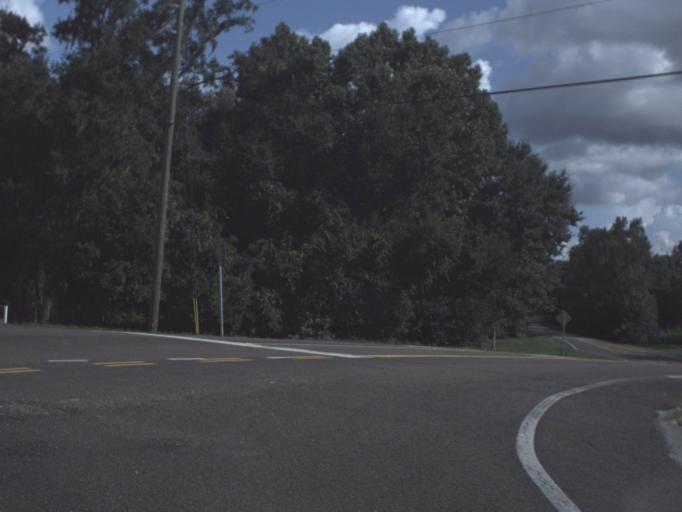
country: US
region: Florida
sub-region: Hernando County
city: South Brooksville
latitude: 28.5444
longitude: -82.4183
